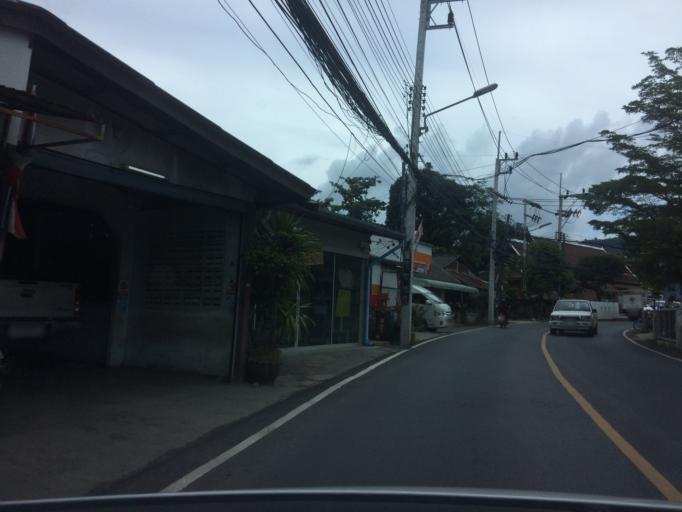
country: TH
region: Phuket
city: Mueang Phuket
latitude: 7.8637
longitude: 98.3587
